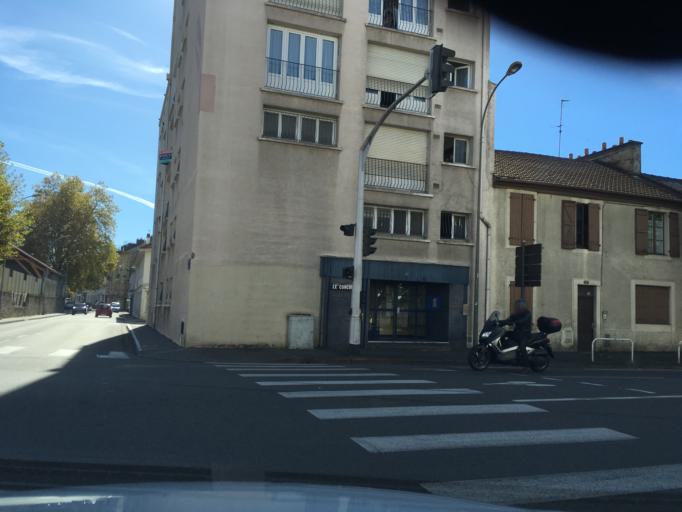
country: FR
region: Aquitaine
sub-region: Departement des Pyrenees-Atlantiques
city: Pau
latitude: 43.3050
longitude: -0.3706
